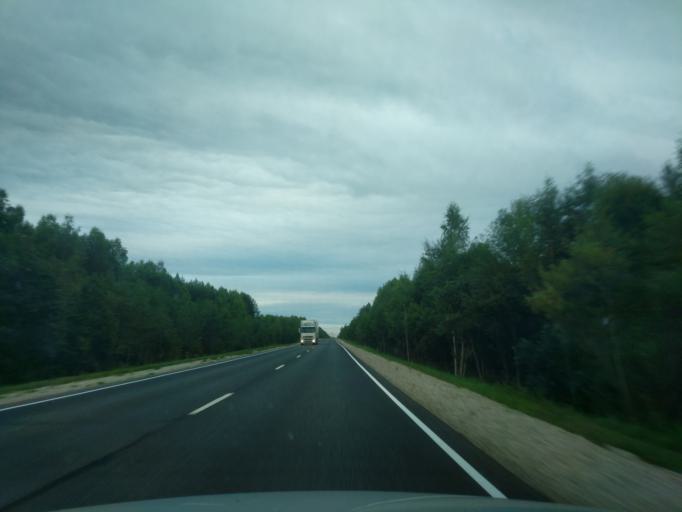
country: RU
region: Kostroma
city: Ponazyrevo
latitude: 58.3237
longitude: 46.5114
